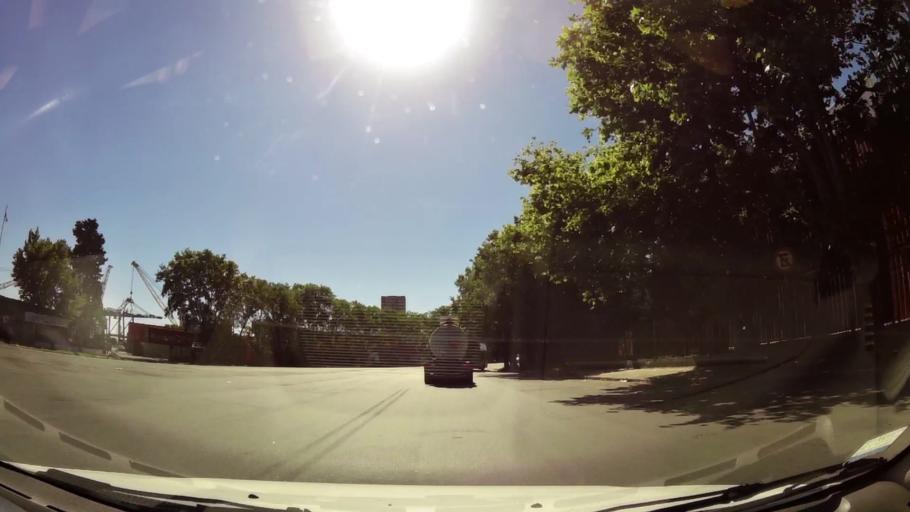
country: AR
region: Buenos Aires F.D.
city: Retiro
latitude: -34.5801
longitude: -58.3769
